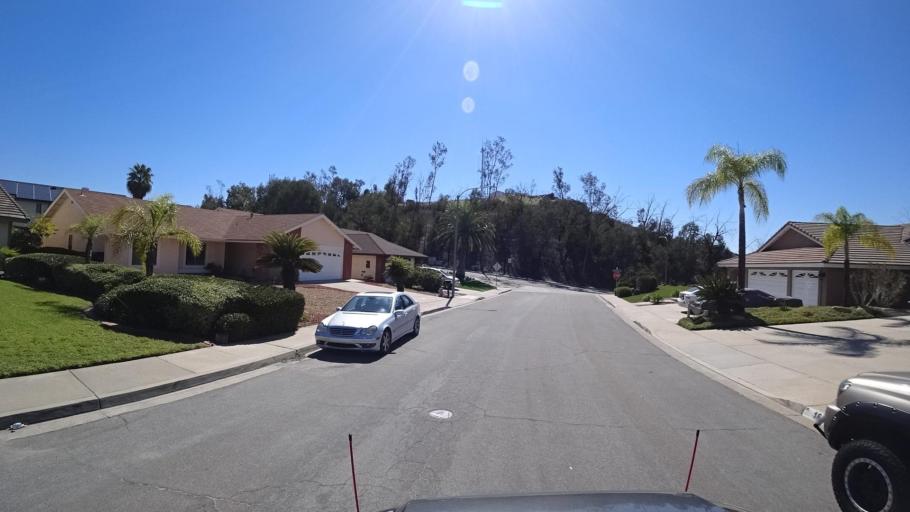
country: US
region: California
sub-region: San Diego County
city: Rancho San Diego
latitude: 32.7515
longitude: -116.9202
